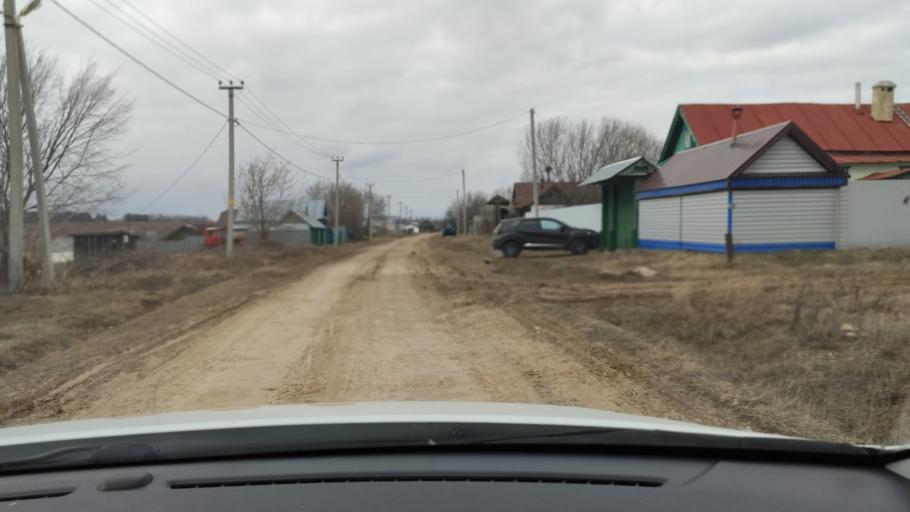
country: RU
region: Tatarstan
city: Vysokaya Gora
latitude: 56.2141
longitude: 49.3129
